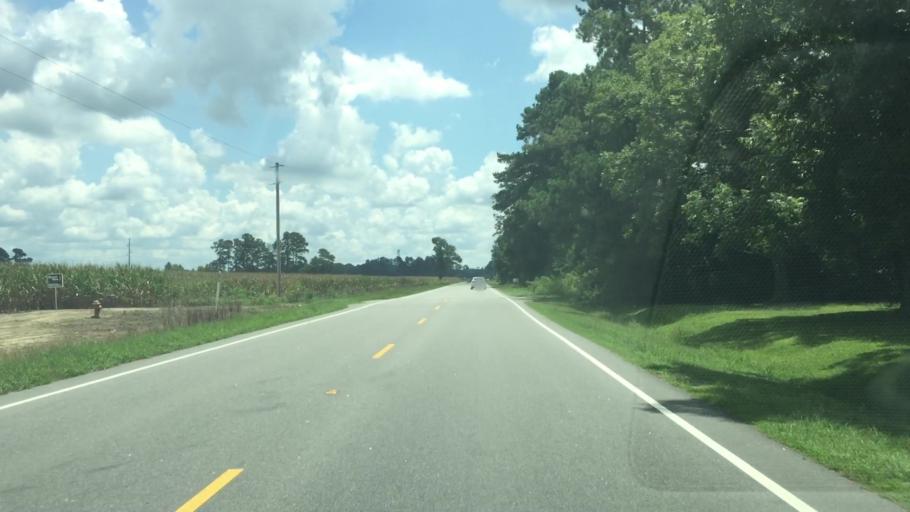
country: US
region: North Carolina
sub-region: Columbus County
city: Chadbourn
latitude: 34.2861
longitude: -78.8213
